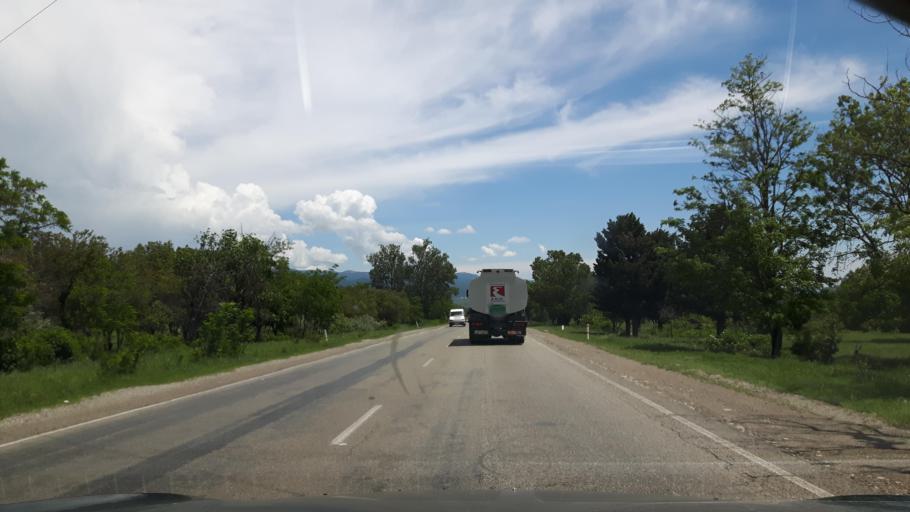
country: GE
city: Didi Lilo
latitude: 41.7048
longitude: 45.1271
